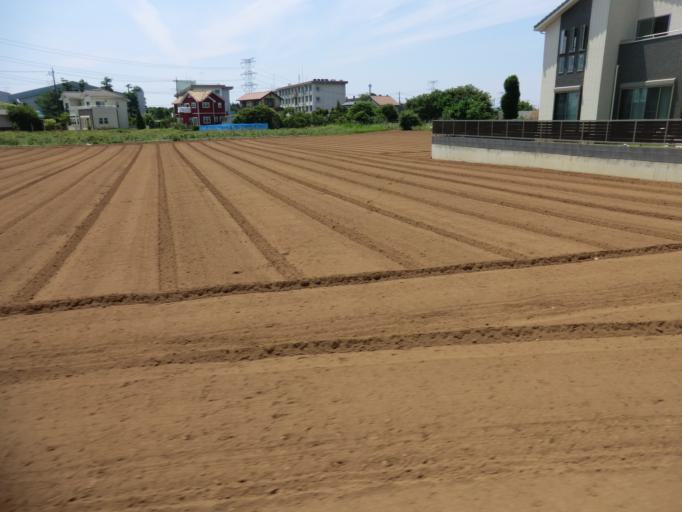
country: JP
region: Ibaraki
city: Ushiku
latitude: 36.0244
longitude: 140.0777
